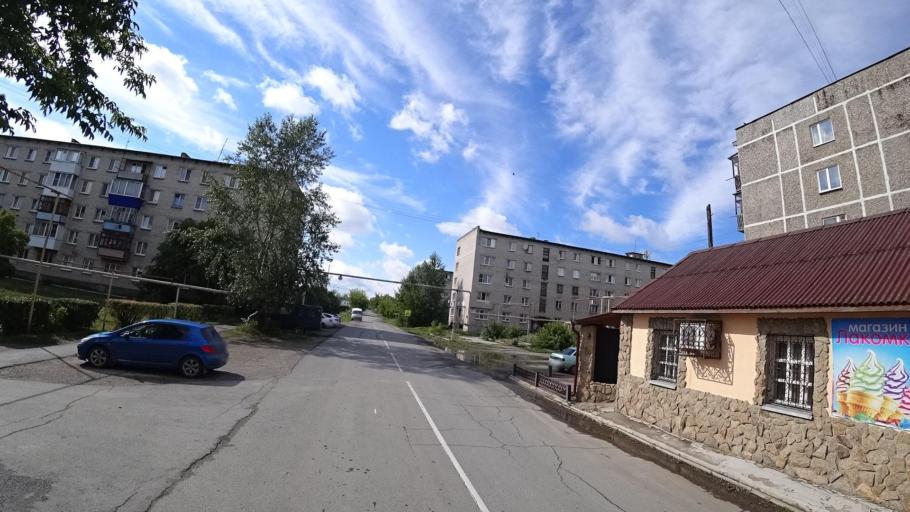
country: RU
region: Sverdlovsk
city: Kamyshlov
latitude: 56.8413
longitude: 62.7184
